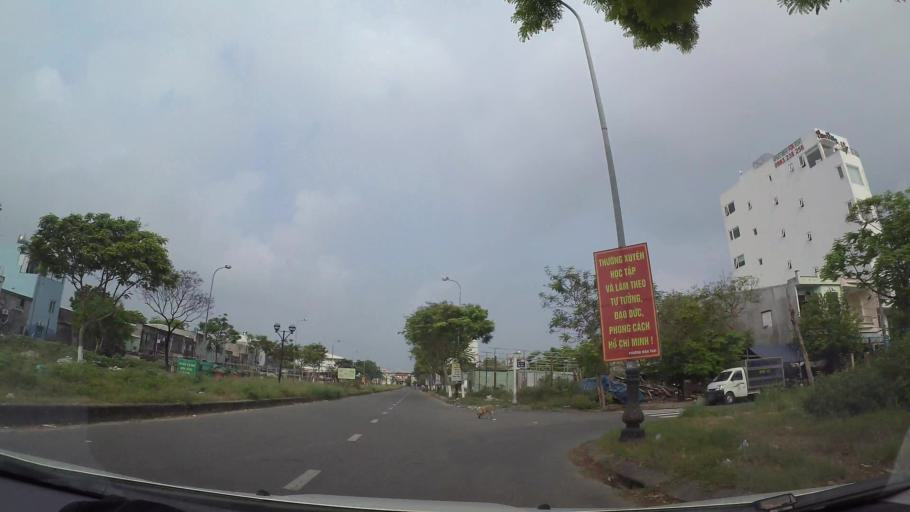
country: VN
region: Da Nang
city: Son Tra
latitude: 16.0880
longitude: 108.2463
